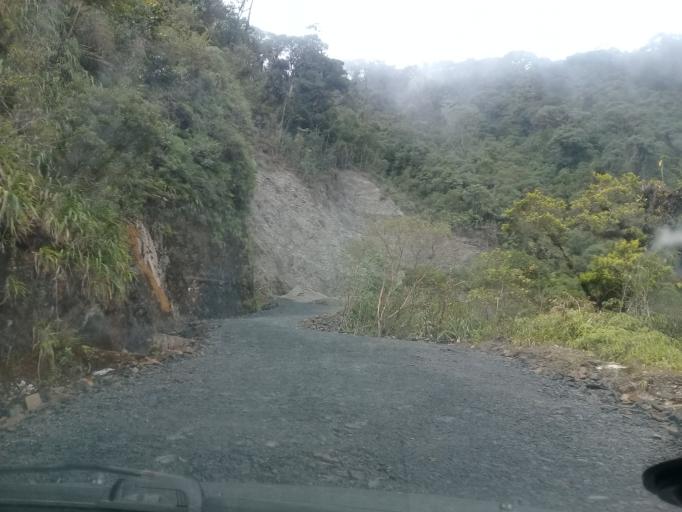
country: CO
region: Cundinamarca
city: Gachala
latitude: 4.7007
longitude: -73.4188
